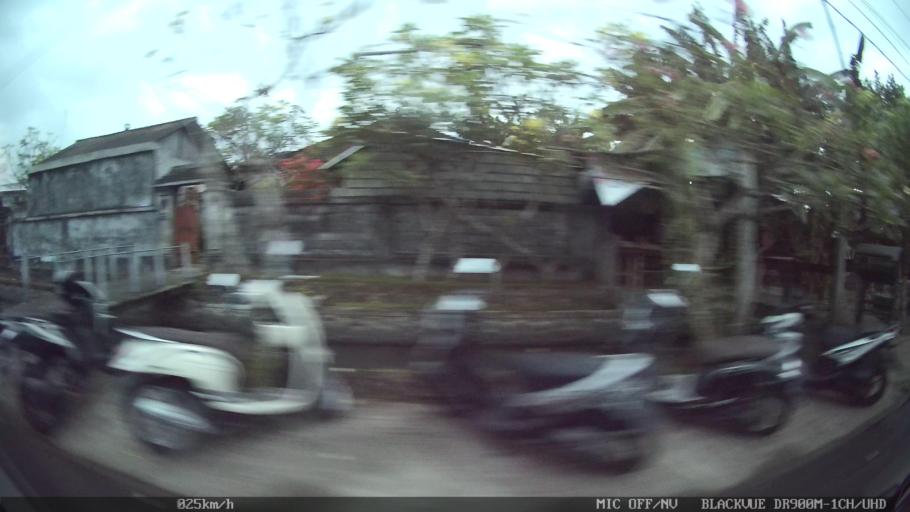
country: ID
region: Bali
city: Banjar Pasekan
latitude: -8.6114
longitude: 115.2863
